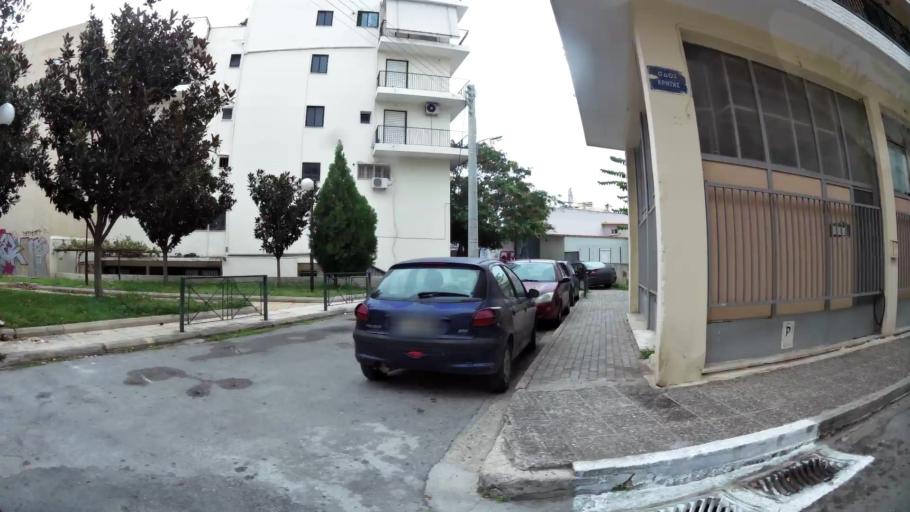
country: GR
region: Attica
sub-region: Nomarchia Athinas
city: Peristeri
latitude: 38.0019
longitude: 23.6824
